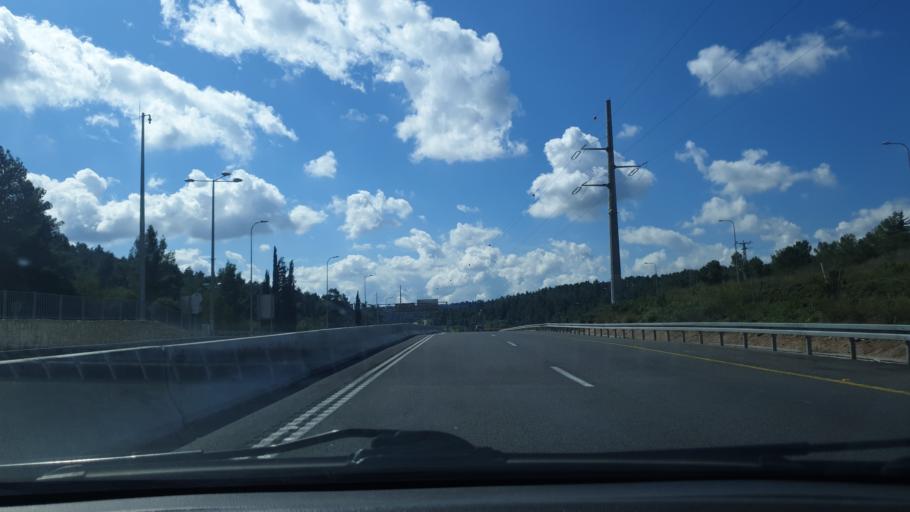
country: IL
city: Mevo horon
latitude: 31.8127
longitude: 35.0213
